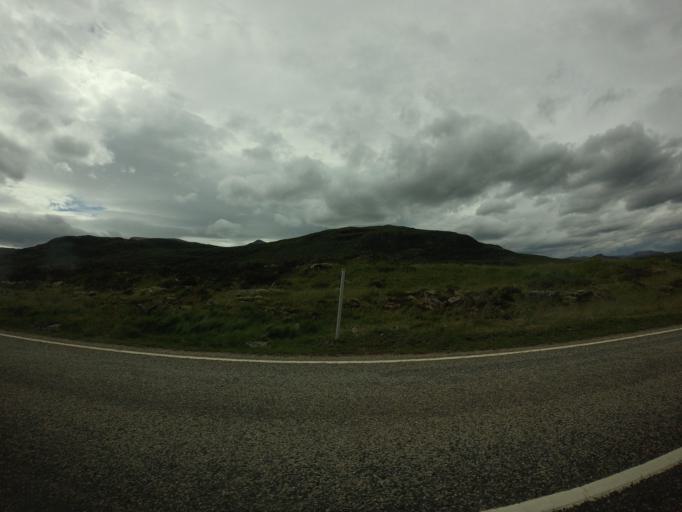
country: GB
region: Scotland
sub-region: Highland
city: Ullapool
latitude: 57.7480
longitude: -4.9853
